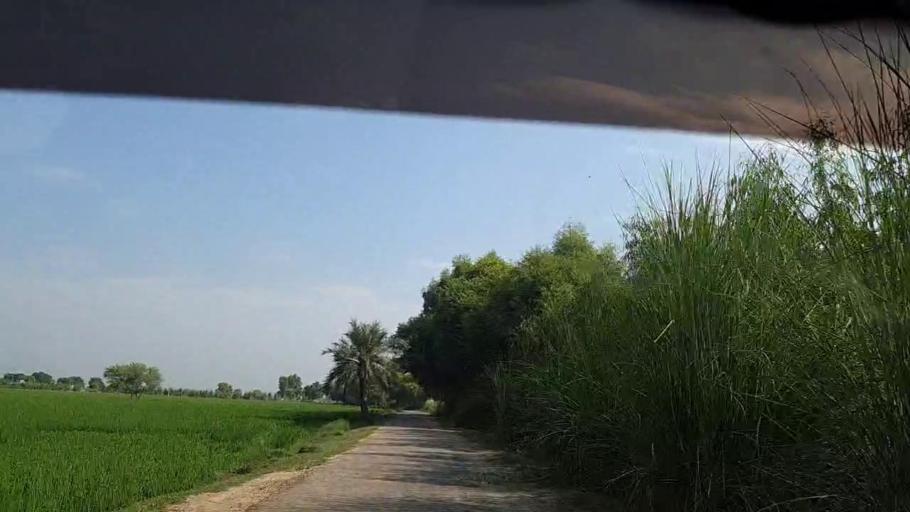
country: PK
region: Sindh
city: Shikarpur
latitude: 28.0943
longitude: 68.6759
